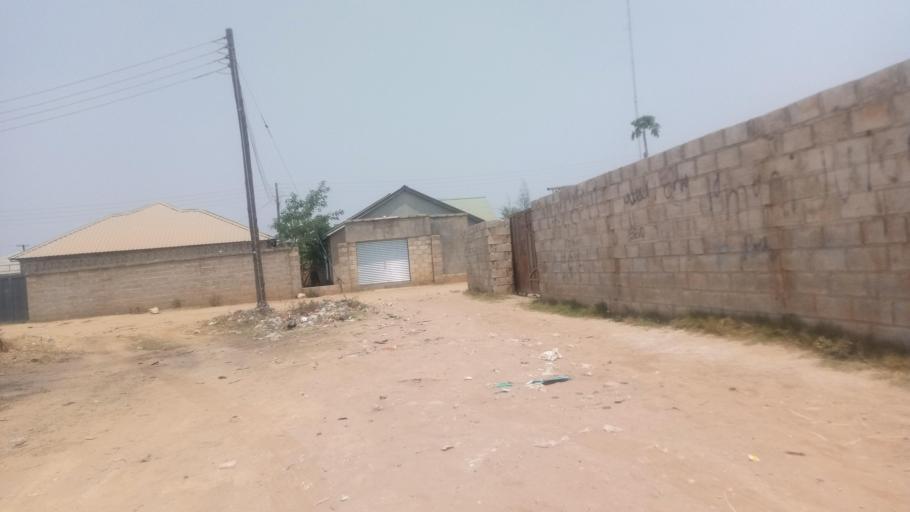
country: ZM
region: Lusaka
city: Lusaka
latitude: -15.4412
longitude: 28.3767
